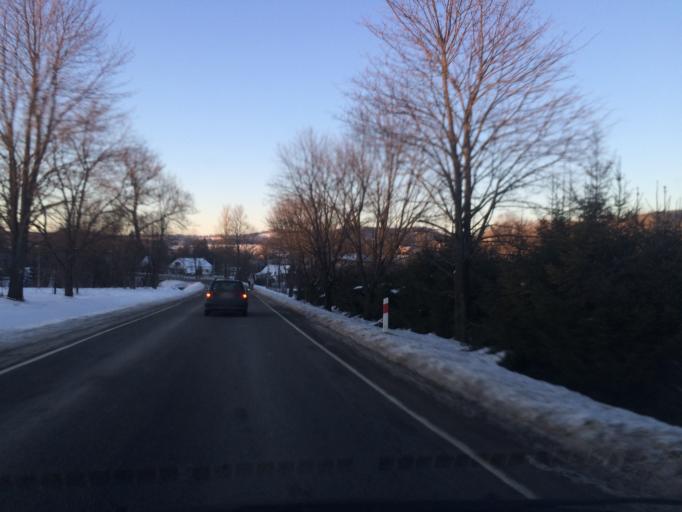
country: PL
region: Subcarpathian Voivodeship
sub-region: Powiat bieszczadzki
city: Czarna
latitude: 49.3186
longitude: 22.6723
